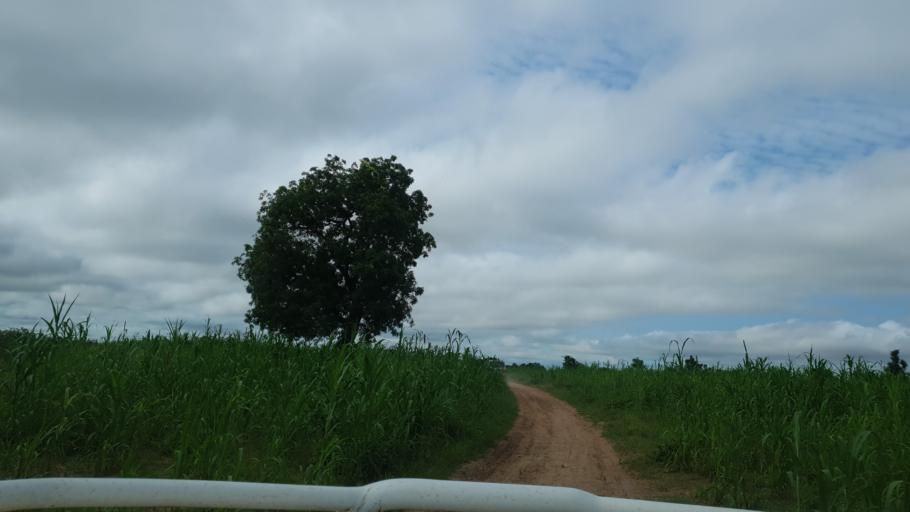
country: ML
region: Segou
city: Baroueli
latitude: 13.4963
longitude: -6.8968
